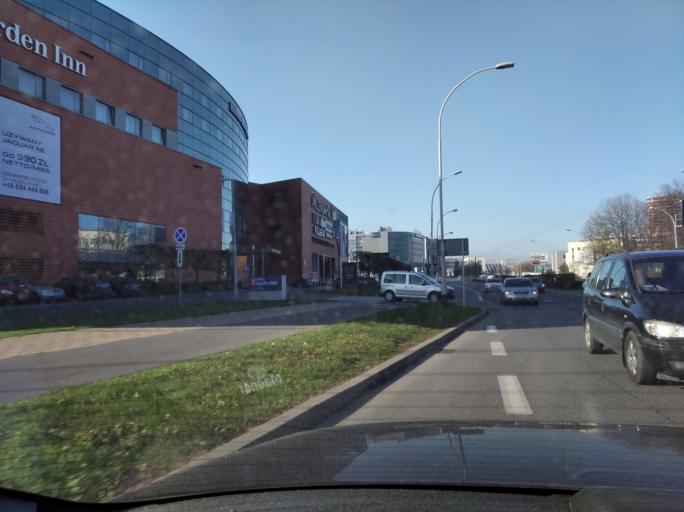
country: PL
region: Subcarpathian Voivodeship
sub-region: Rzeszow
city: Rzeszow
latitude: 50.0283
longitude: 22.0151
